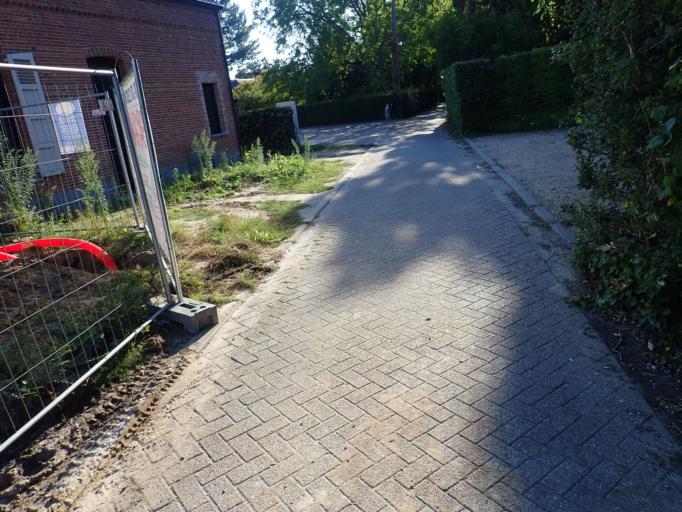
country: BE
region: Flanders
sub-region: Provincie Antwerpen
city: Heist-op-den-Berg
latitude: 51.1028
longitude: 4.7271
